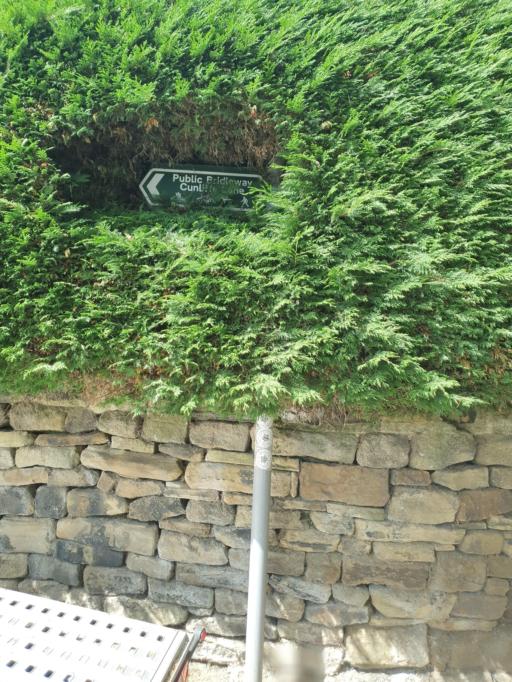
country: GB
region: England
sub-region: City and Borough of Leeds
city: Guiseley
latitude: 53.8576
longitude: -1.7279
